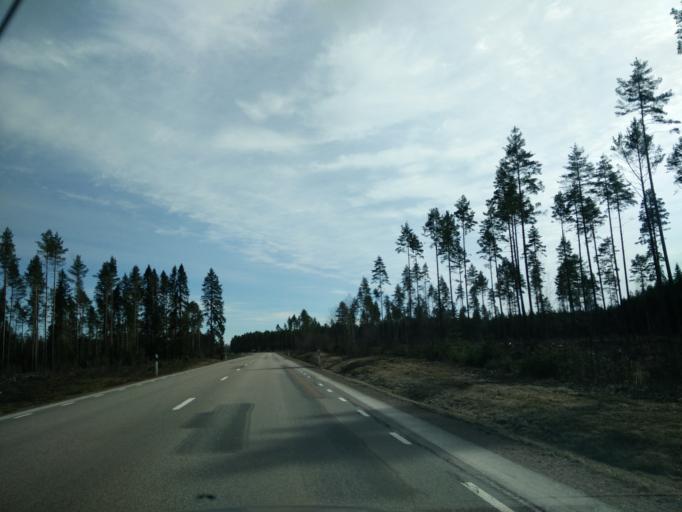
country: SE
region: Vaermland
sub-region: Hagfors Kommun
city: Hagfors
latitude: 60.0188
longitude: 13.5924
